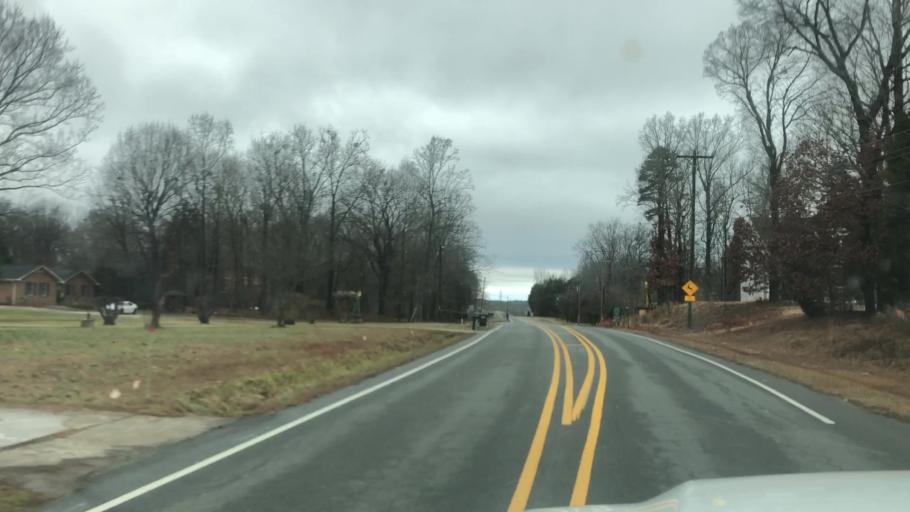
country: US
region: North Carolina
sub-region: Mecklenburg County
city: Mint Hill
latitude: 35.2403
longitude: -80.6734
